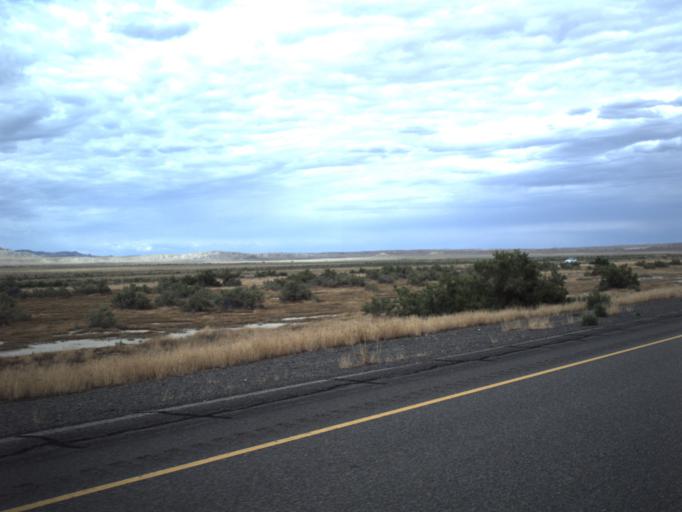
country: US
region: Utah
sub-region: Grand County
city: Moab
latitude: 38.9418
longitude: -109.5905
